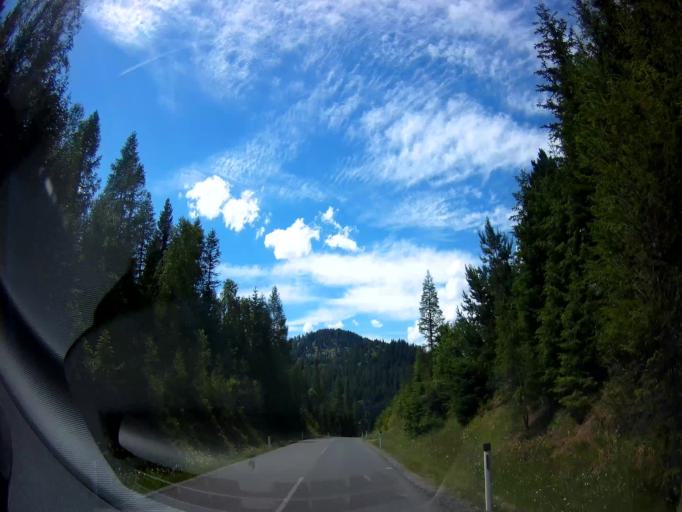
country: AT
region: Carinthia
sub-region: Politischer Bezirk Sankt Veit an der Glan
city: Glodnitz
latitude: 46.9468
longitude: 14.0280
